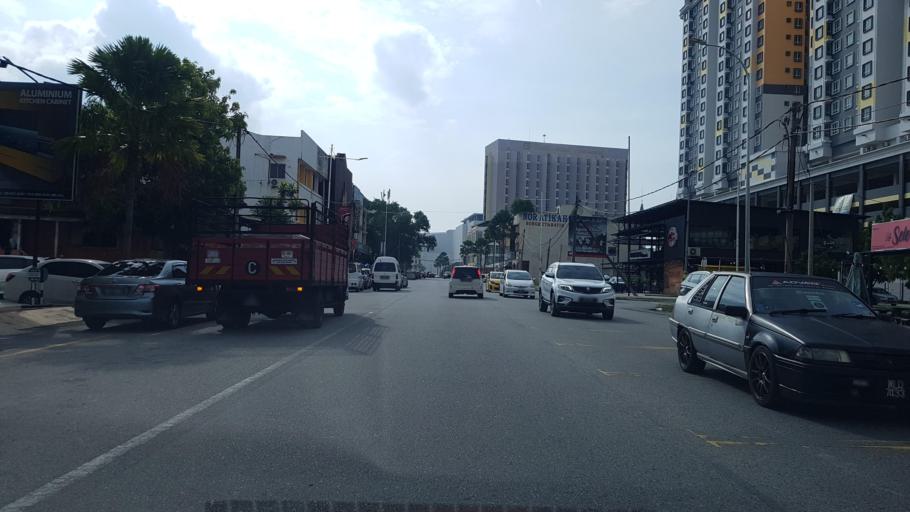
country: MY
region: Terengganu
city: Kuala Terengganu
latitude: 5.3330
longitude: 103.1481
